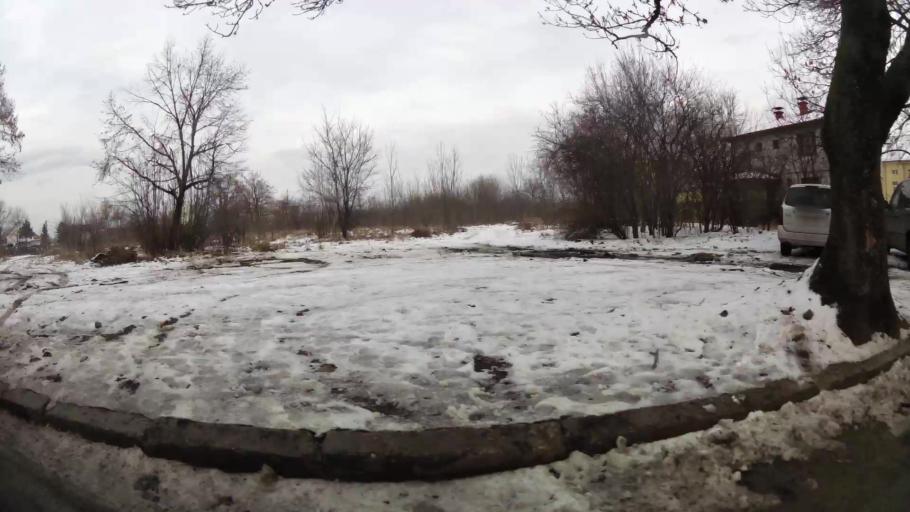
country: BG
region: Sofia-Capital
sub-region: Stolichna Obshtina
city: Sofia
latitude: 42.7189
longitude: 23.3465
